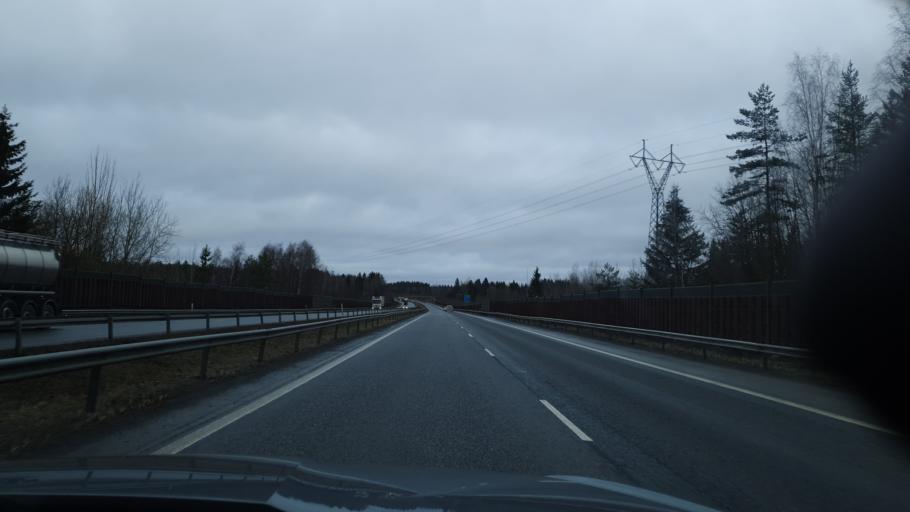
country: FI
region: Pirkanmaa
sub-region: Tampere
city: Lempaeaelae
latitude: 61.3858
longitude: 23.7900
